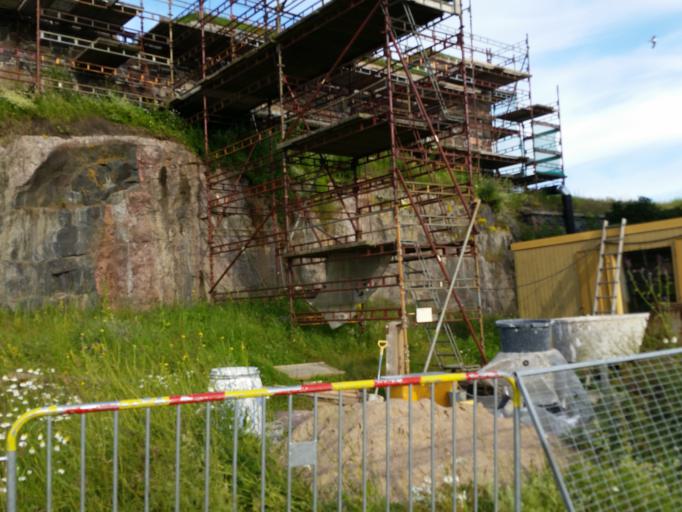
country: FI
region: Uusimaa
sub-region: Helsinki
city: Helsinki
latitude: 60.1390
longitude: 24.9882
